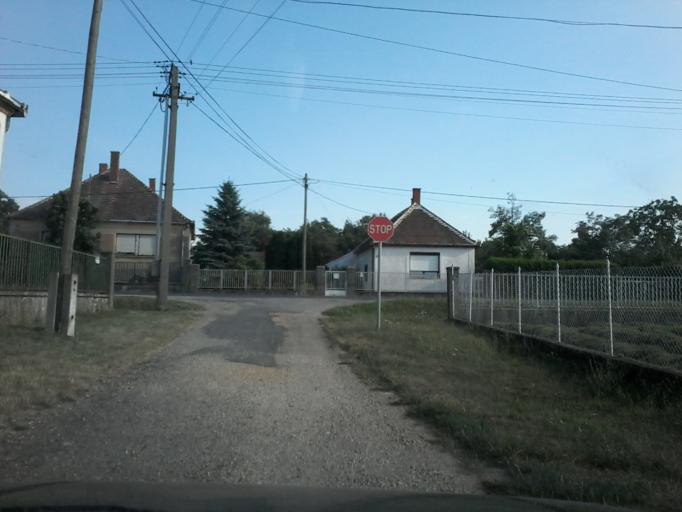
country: HU
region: Vas
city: Sarvar
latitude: 47.2199
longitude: 17.0098
